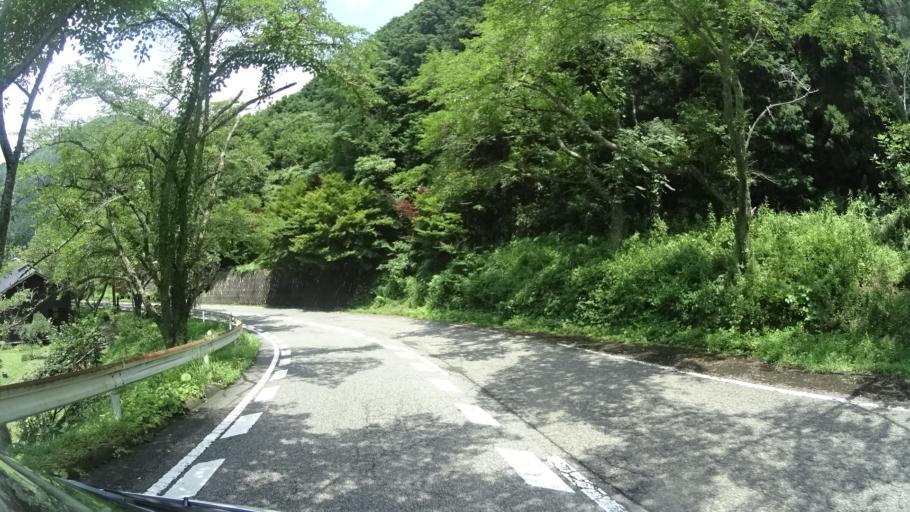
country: JP
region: Hyogo
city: Sasayama
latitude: 35.1752
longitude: 135.2465
